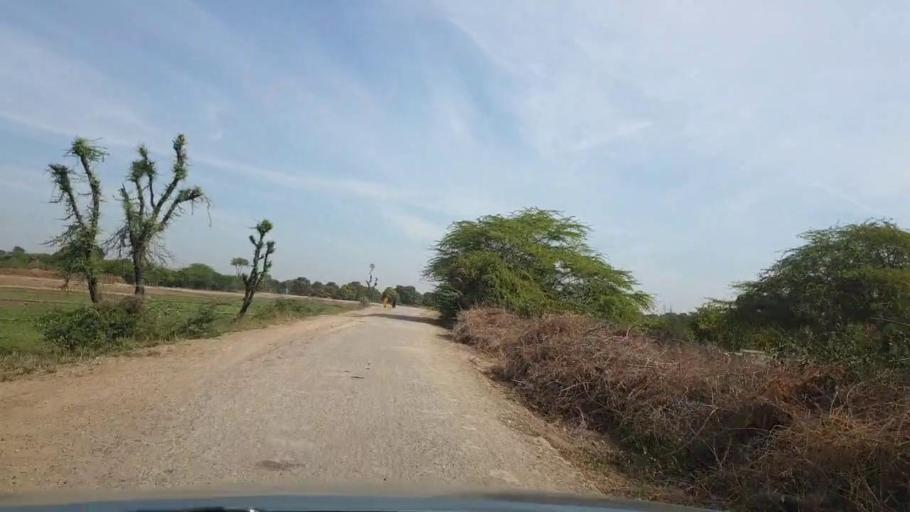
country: PK
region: Sindh
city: Kunri
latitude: 25.1638
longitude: 69.5991
